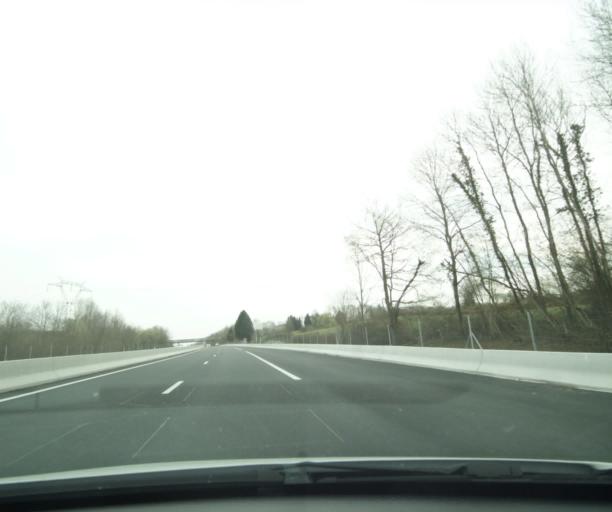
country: FR
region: Aquitaine
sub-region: Departement des Pyrenees-Atlantiques
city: Lahonce
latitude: 43.4477
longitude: -1.3744
